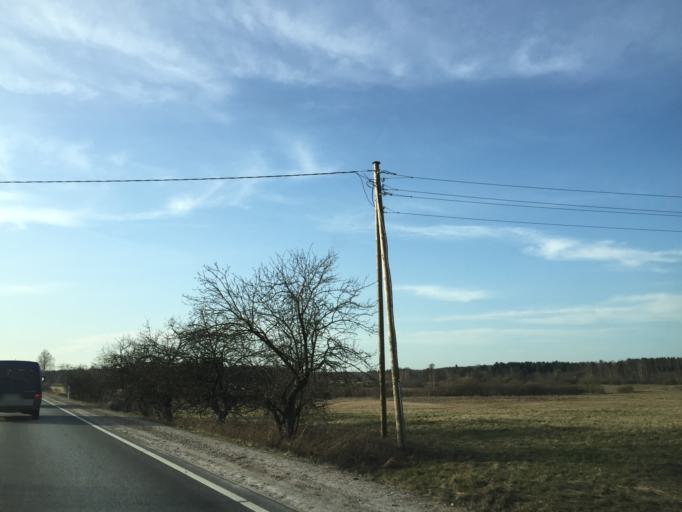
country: LV
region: Ikskile
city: Ikskile
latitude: 56.8675
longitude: 24.5507
